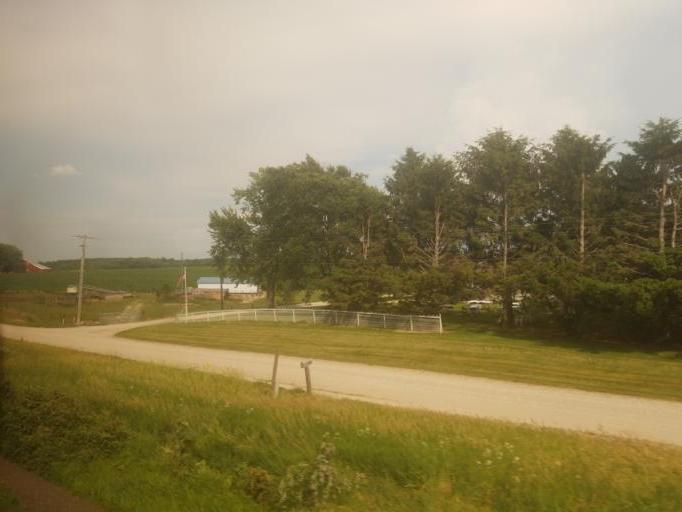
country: US
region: Illinois
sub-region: Henry County
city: Galva
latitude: 41.0978
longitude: -90.1871
